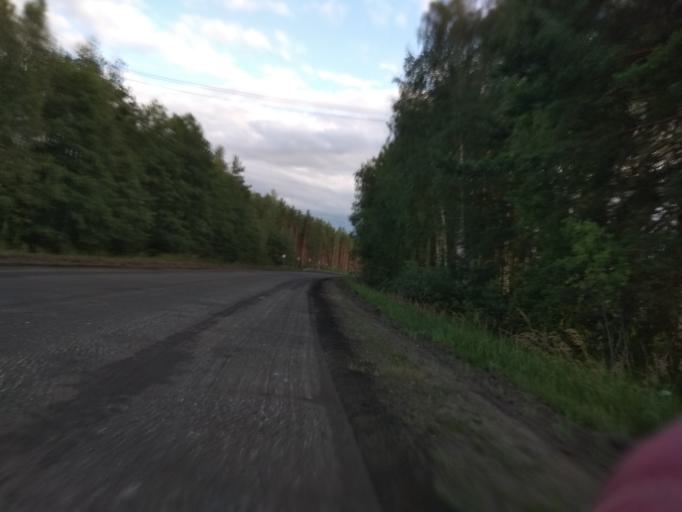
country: RU
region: Moskovskaya
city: Misheronskiy
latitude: 55.6472
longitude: 39.7573
